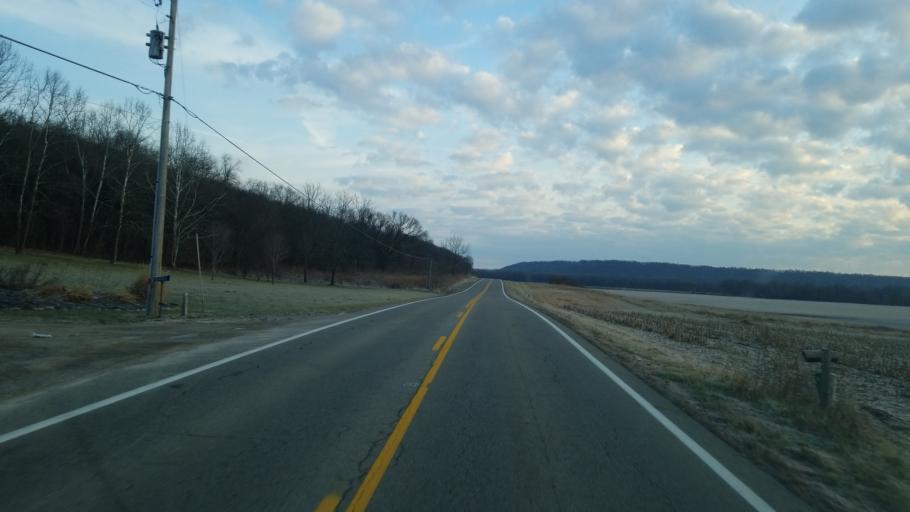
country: US
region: Ohio
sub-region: Ross County
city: Frankfort
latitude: 39.2601
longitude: -83.1816
